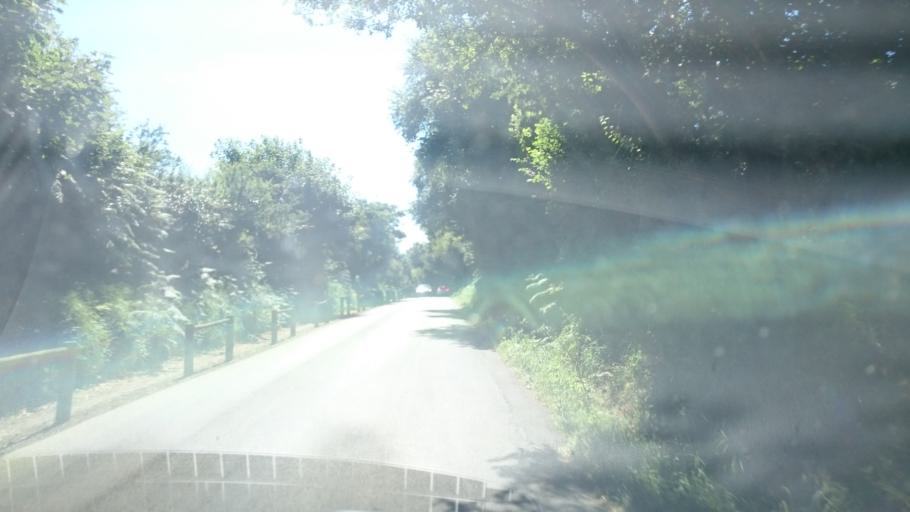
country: FR
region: Lower Normandy
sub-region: Departement de la Manche
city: Les Pieux
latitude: 49.5097
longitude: -1.8299
